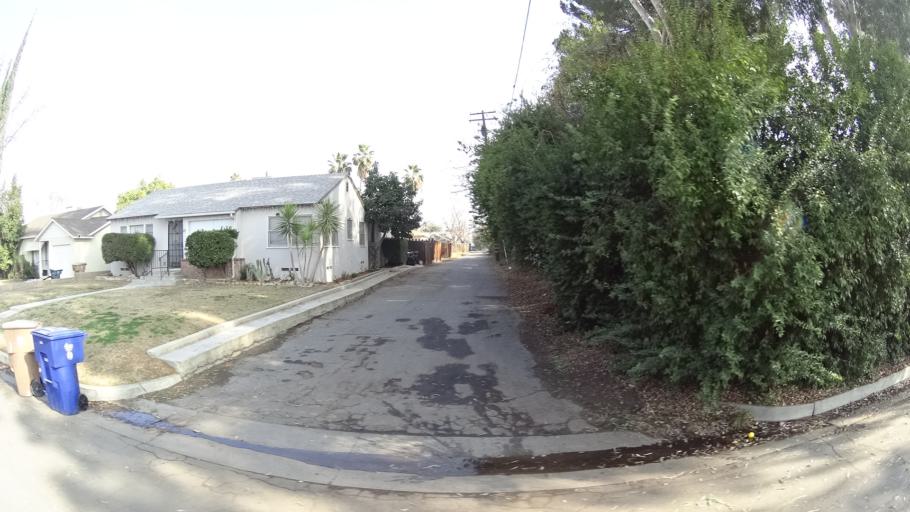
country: US
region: California
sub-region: Kern County
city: Bakersfield
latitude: 35.3560
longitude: -119.0310
